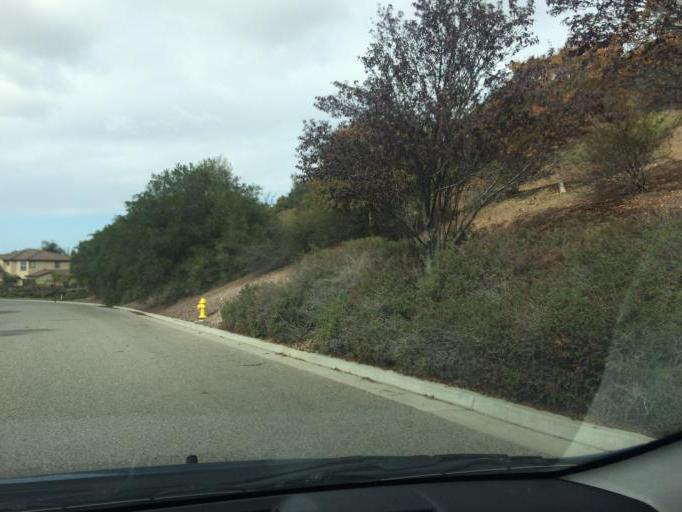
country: US
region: California
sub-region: Santa Clara County
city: Seven Trees
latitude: 37.2826
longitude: -121.7915
